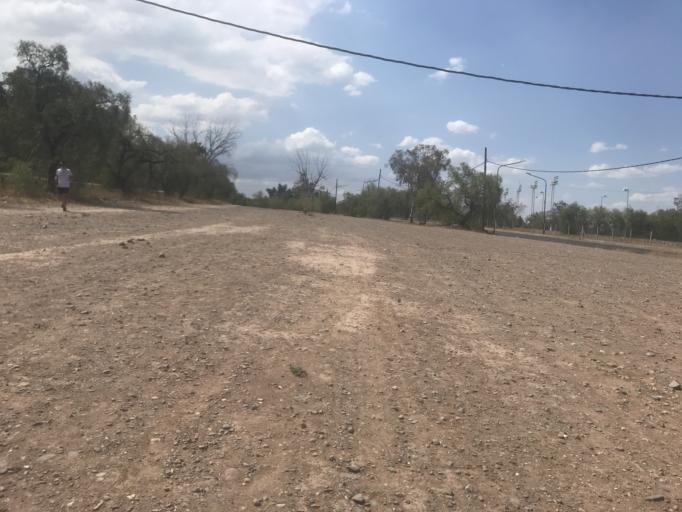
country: AR
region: Mendoza
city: Mendoza
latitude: -32.8875
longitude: -68.8847
